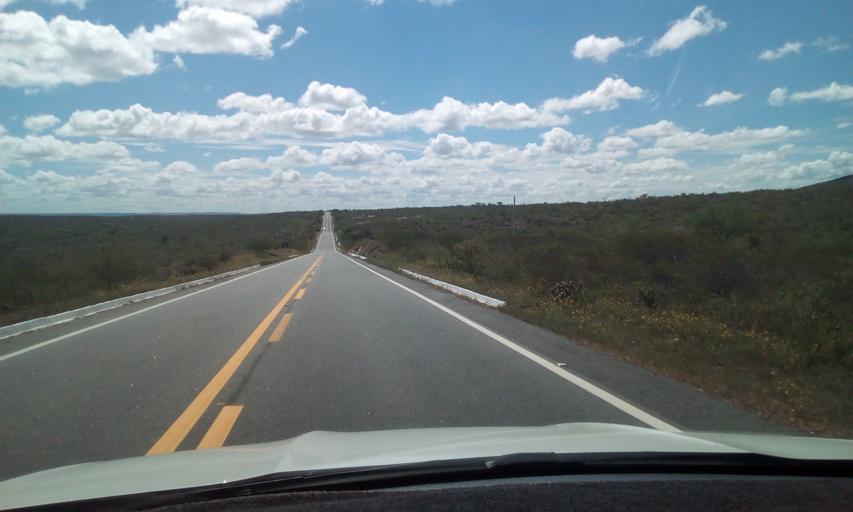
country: BR
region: Paraiba
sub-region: Arara
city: Arara
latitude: -6.8551
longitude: -35.9266
